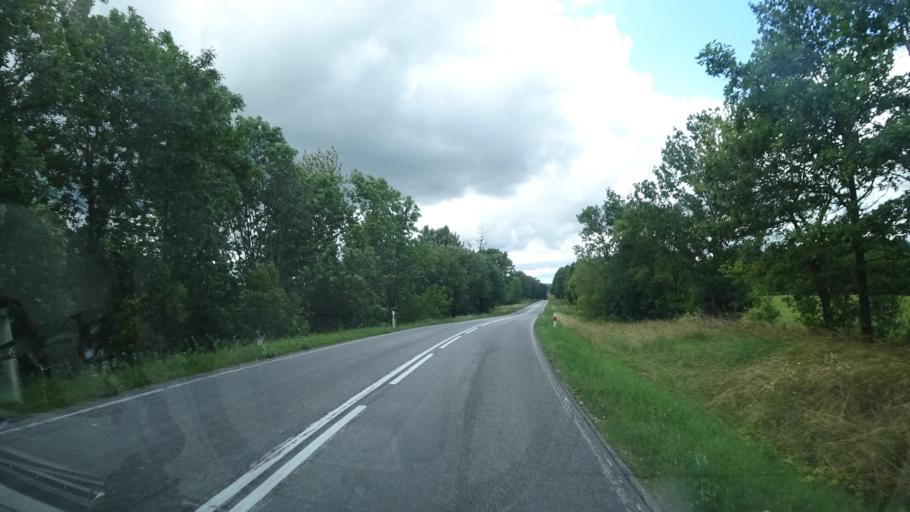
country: PL
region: Warmian-Masurian Voivodeship
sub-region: Powiat goldapski
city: Goldap
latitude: 54.2169
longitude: 22.2253
